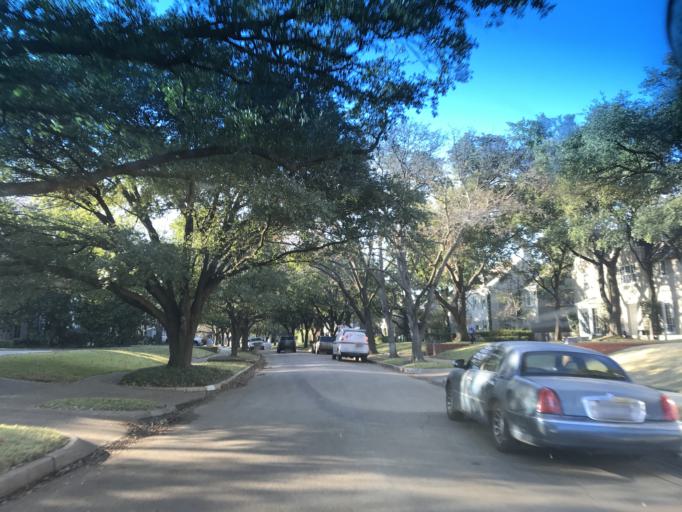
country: US
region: Texas
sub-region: Dallas County
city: Highland Park
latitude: 32.8276
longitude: -96.8051
